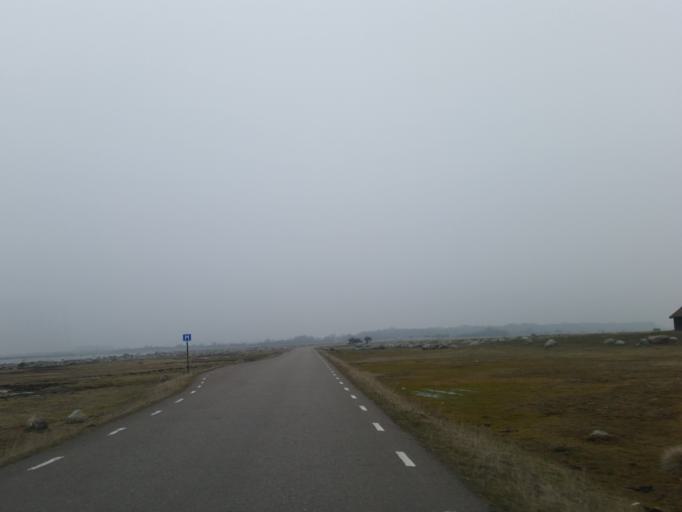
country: SE
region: Kalmar
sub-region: Morbylanga Kommun
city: Moerbylanga
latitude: 56.2040
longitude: 16.4020
